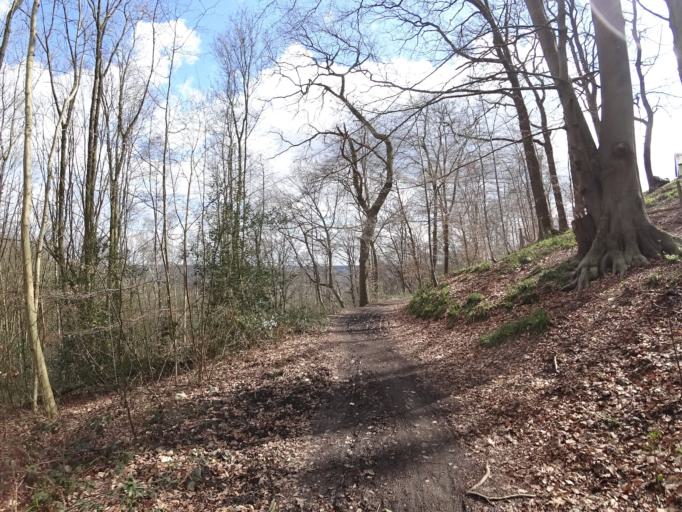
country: BE
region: Wallonia
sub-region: Province de Namur
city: Namur
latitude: 50.4526
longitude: 4.8546
